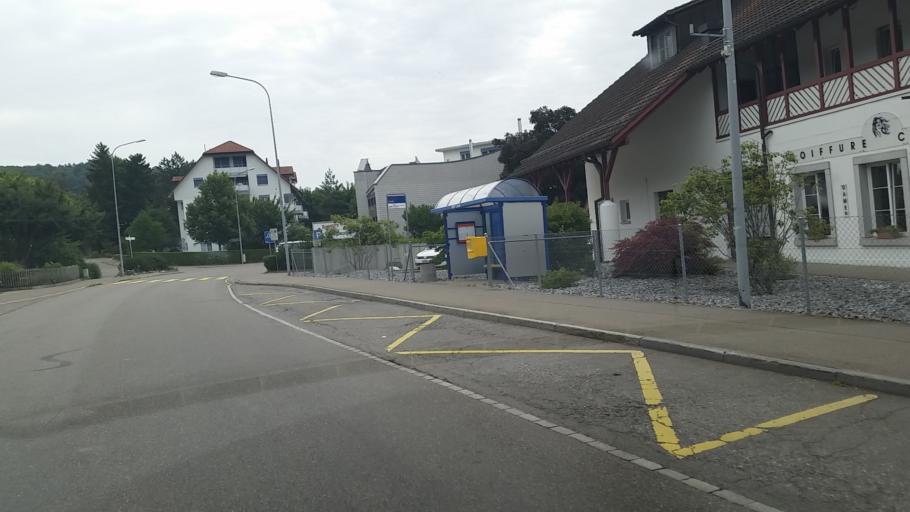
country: CH
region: Zurich
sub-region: Bezirk Dielsdorf
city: Daellikon / Daellikon (Dorf)
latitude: 47.4584
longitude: 8.4401
